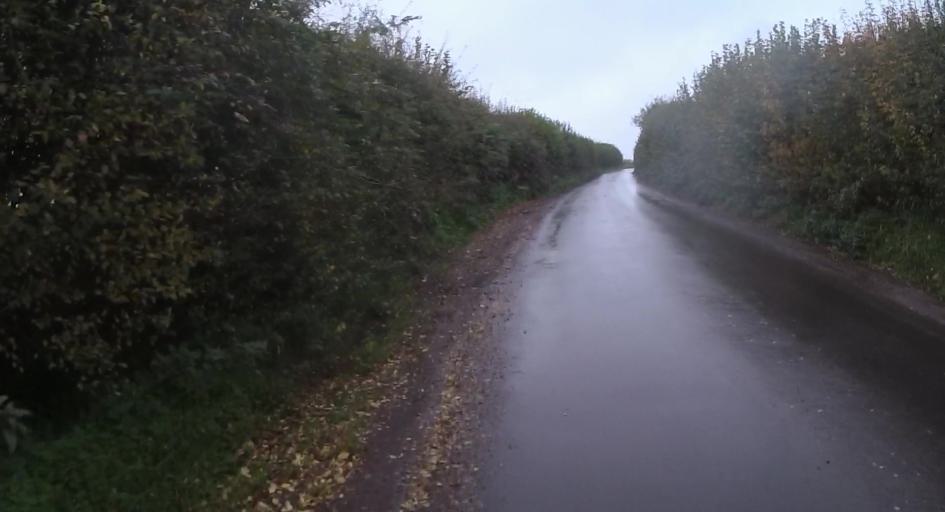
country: GB
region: England
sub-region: Surrey
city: Farnham
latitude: 51.2089
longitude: -0.8548
